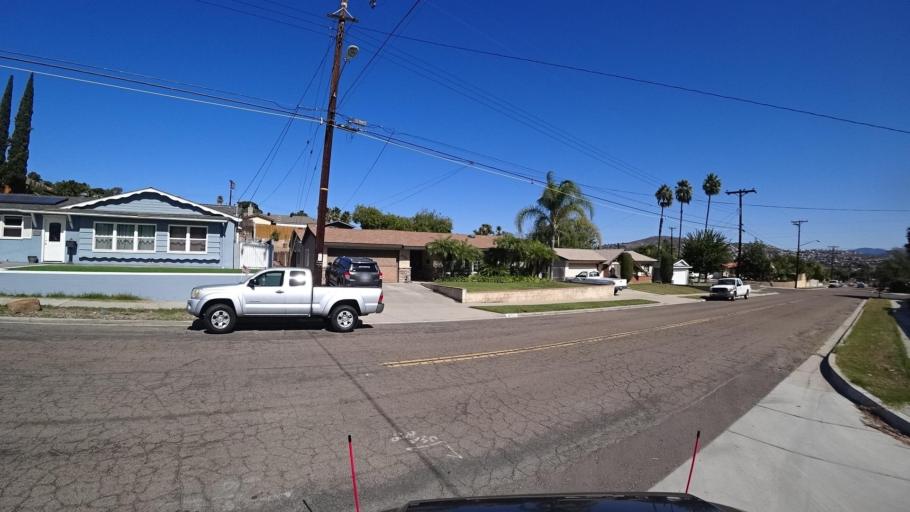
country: US
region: California
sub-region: San Diego County
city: La Presa
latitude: 32.7039
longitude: -117.0196
